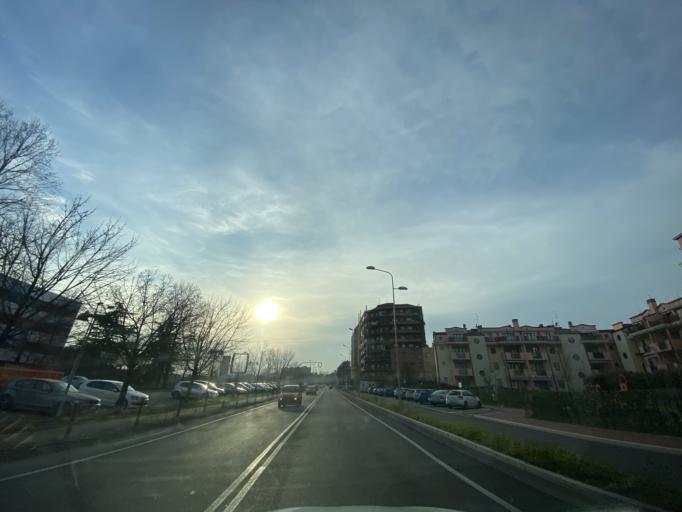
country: IT
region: Lombardy
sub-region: Citta metropolitana di Milano
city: Vimodrone
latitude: 45.5127
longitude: 9.2899
